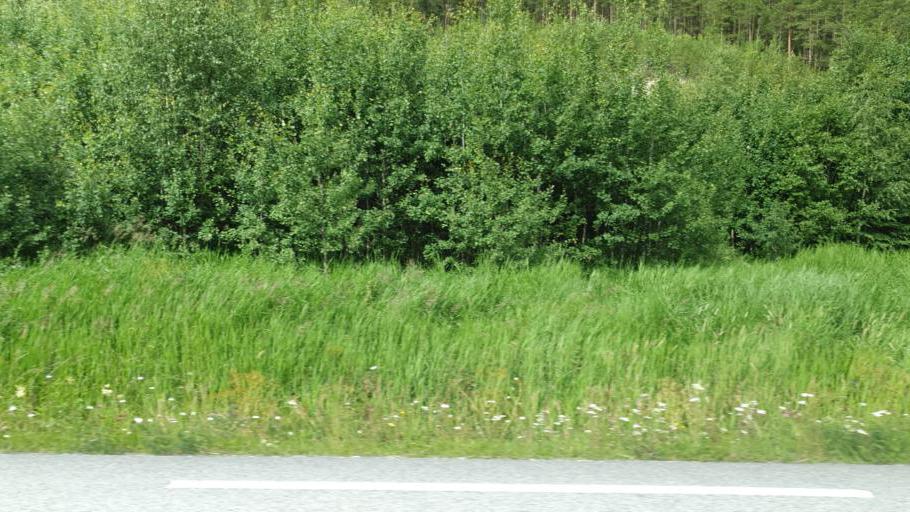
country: NO
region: Oppland
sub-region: Sel
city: Otta
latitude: 61.8434
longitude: 9.3795
